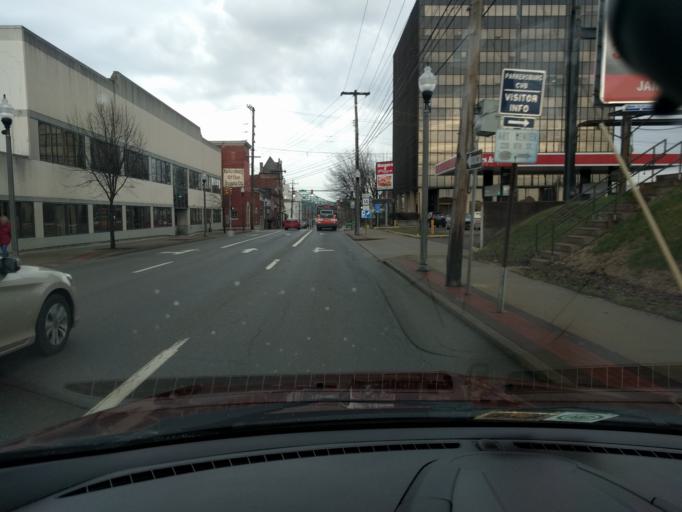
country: US
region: West Virginia
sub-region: Wood County
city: Parkersburg
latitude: 39.2643
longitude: -81.5590
